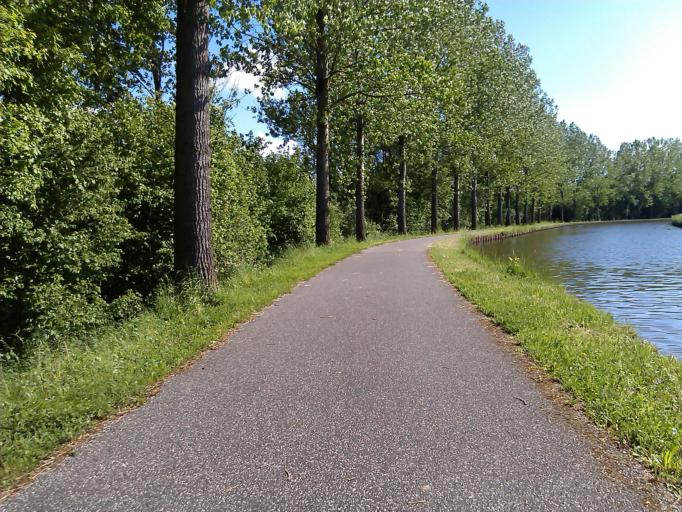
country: FR
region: Bourgogne
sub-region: Departement de Saone-et-Loire
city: Ecuisses
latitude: 46.7650
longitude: 4.5242
